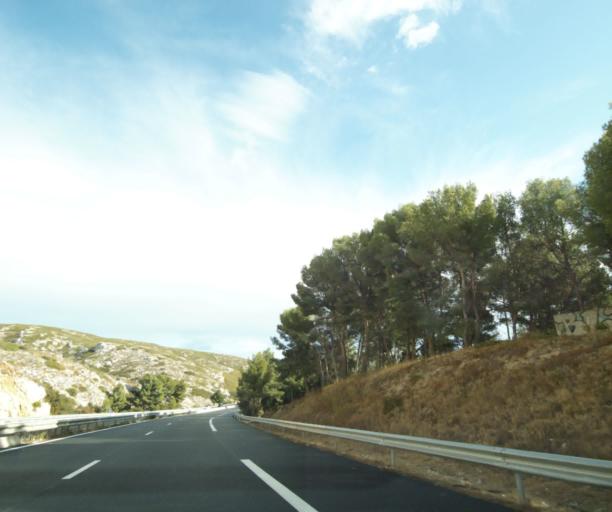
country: FR
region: Provence-Alpes-Cote d'Azur
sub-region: Departement des Bouches-du-Rhone
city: Sausset-les-Pins
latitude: 43.3436
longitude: 5.1259
